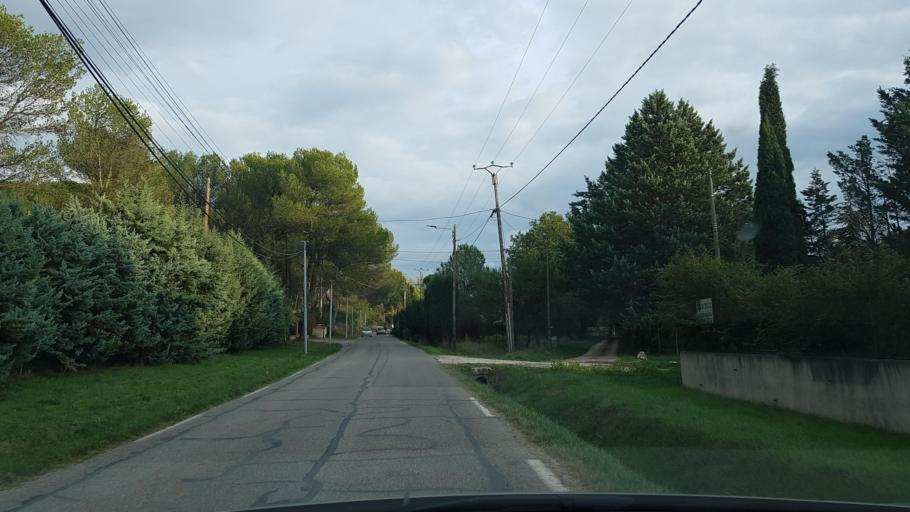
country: FR
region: Provence-Alpes-Cote d'Azur
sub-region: Departement des Bouches-du-Rhone
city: Cabries
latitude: 43.4495
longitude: 5.3640
